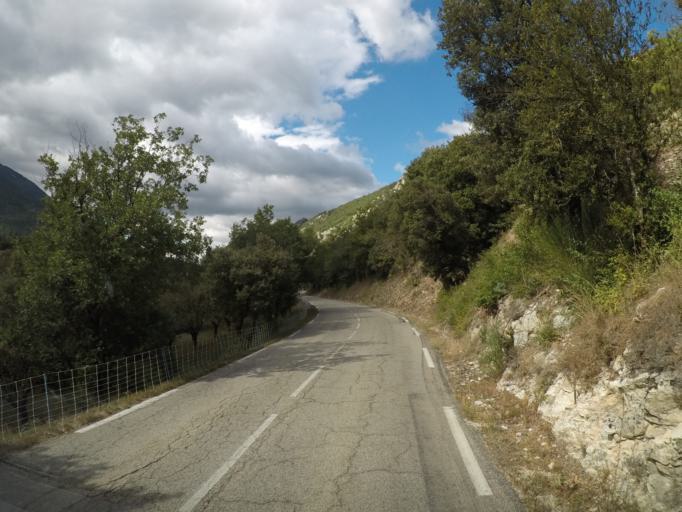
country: FR
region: Rhone-Alpes
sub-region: Departement de la Drome
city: Buis-les-Baronnies
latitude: 44.1910
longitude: 5.3330
